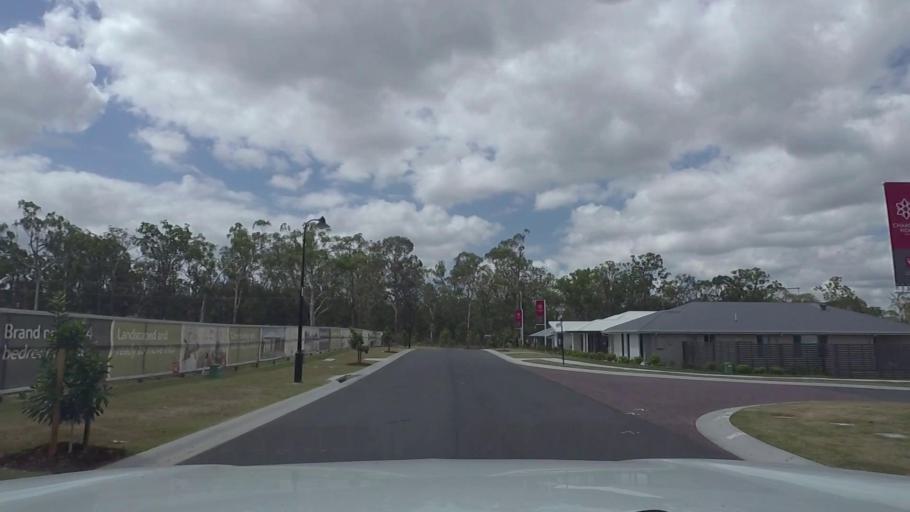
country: AU
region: Queensland
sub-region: Logan
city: Logan Reserve
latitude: -27.7185
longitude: 153.0886
